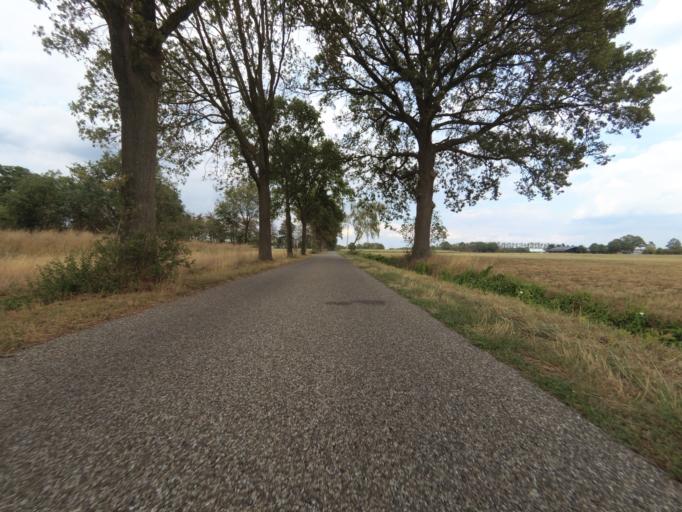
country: NL
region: Overijssel
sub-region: Gemeente Hof van Twente
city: Delden
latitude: 52.2232
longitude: 6.7440
